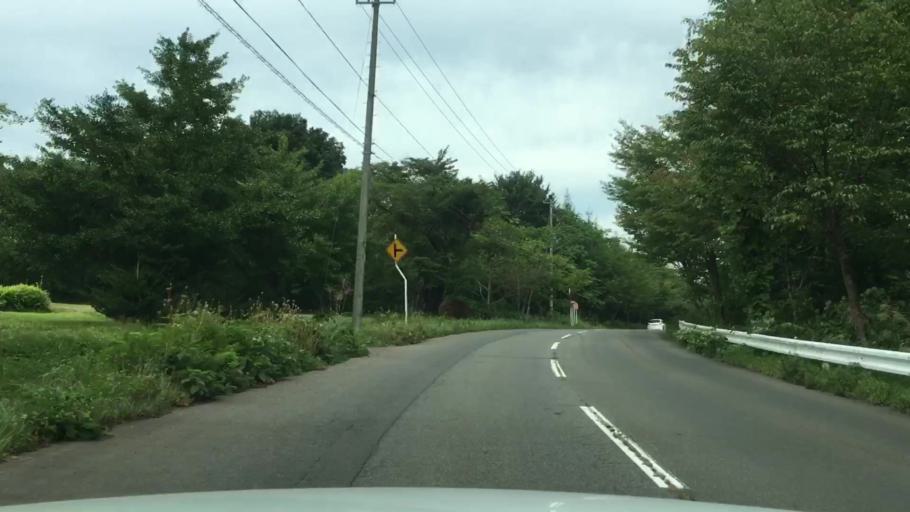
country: JP
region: Aomori
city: Shimokizukuri
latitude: 40.6877
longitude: 140.3632
